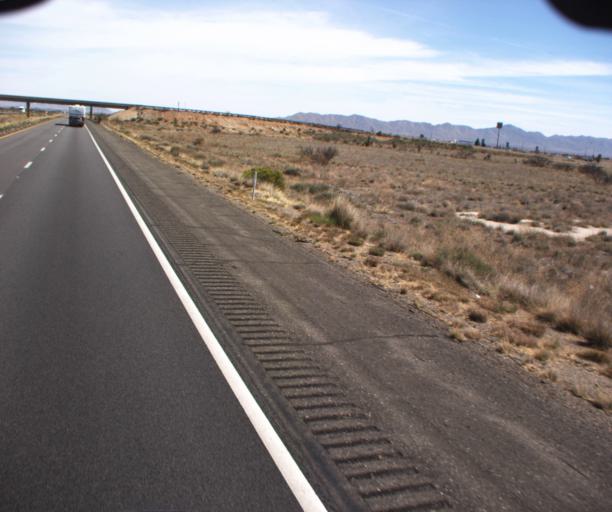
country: US
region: Arizona
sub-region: Cochise County
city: Willcox
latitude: 32.2204
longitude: -109.8795
